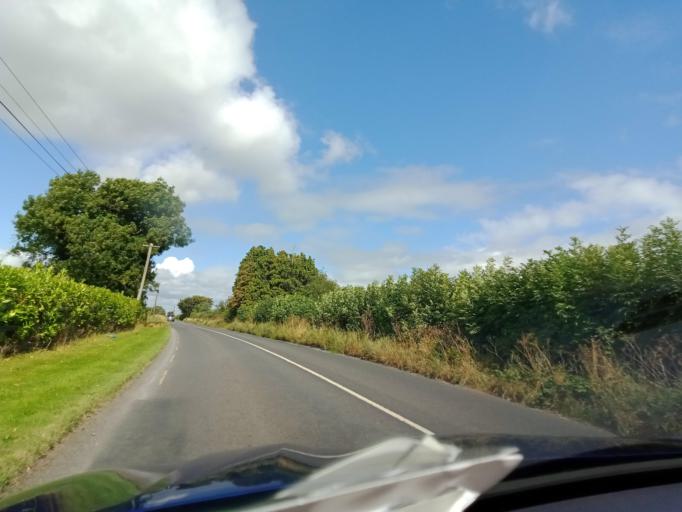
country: IE
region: Leinster
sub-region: Laois
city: Portlaoise
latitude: 52.9591
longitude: -7.2986
